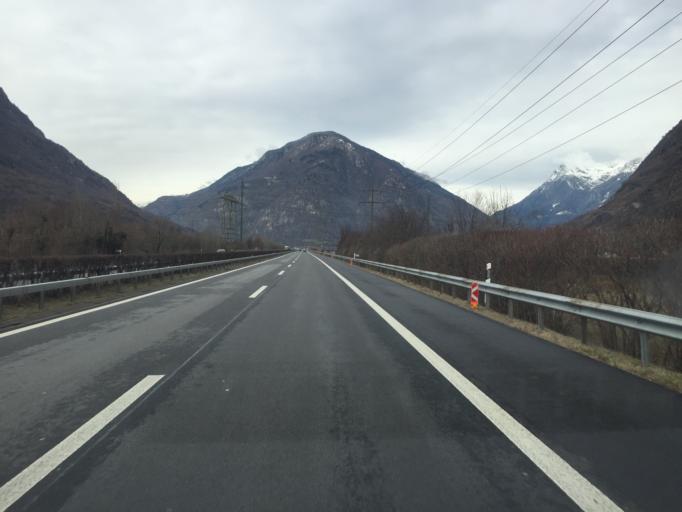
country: CH
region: Ticino
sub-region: Riviera District
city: Lodrino
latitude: 46.3296
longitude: 8.9778
